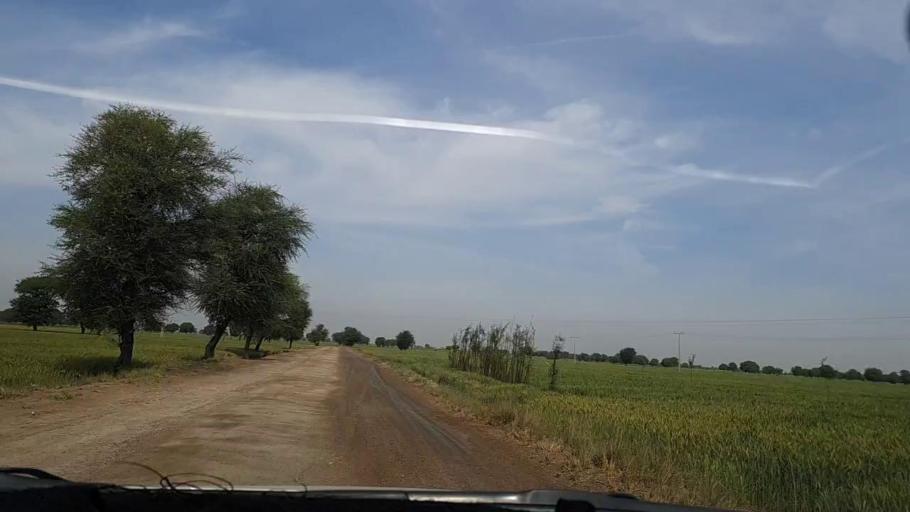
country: PK
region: Sindh
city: Dhoro Naro
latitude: 25.4480
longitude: 69.4973
